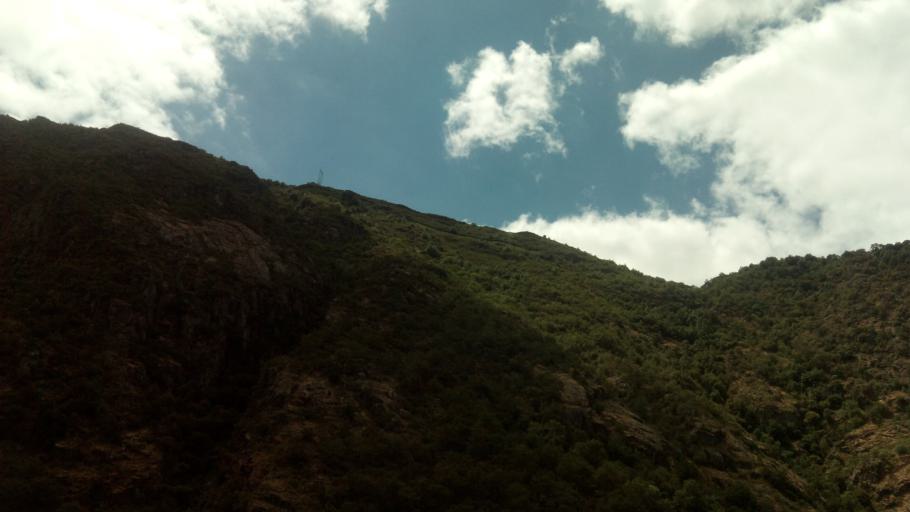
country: ES
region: Galicia
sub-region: Provincia de Lugo
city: Sober
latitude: 42.3849
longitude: -7.6133
